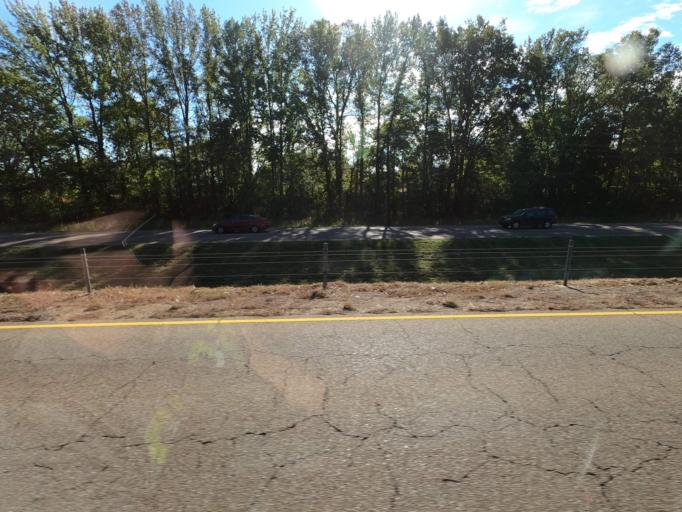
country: US
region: Tennessee
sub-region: Tipton County
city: Brighton
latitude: 35.5013
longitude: -89.7188
